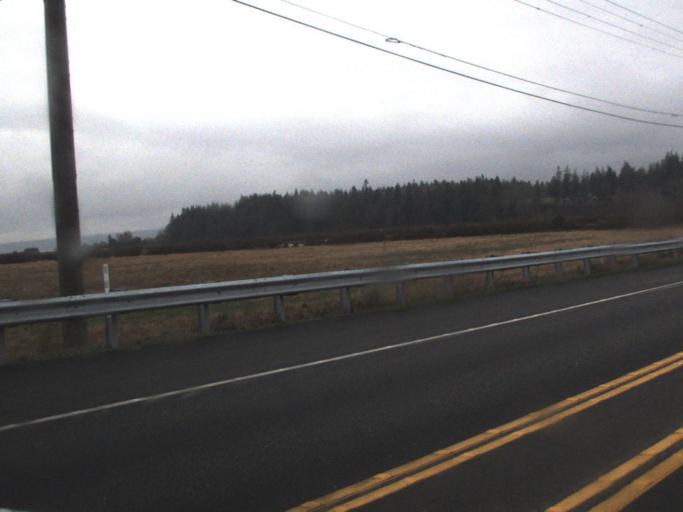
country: US
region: Washington
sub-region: Snohomish County
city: Stanwood
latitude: 48.2397
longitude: -122.3878
